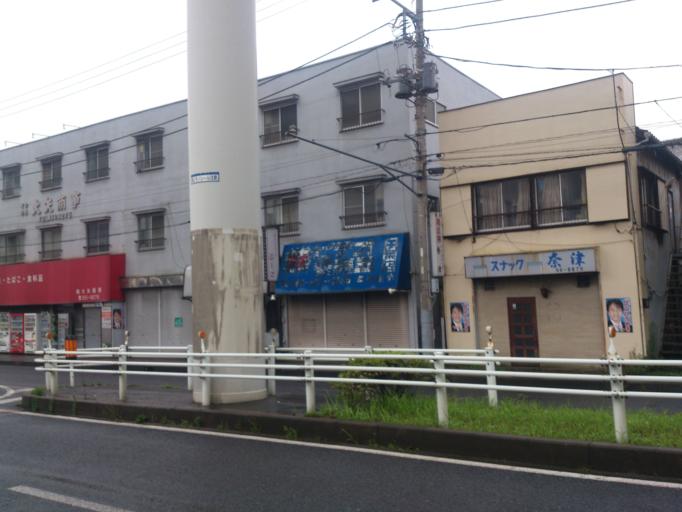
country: JP
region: Chiba
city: Chiba
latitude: 35.6269
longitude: 140.1146
